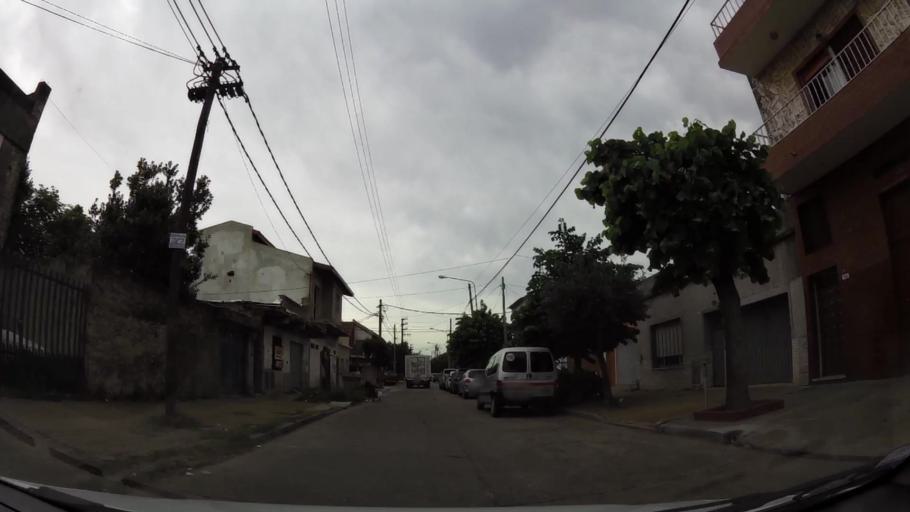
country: AR
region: Buenos Aires
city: San Justo
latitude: -34.6680
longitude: -58.5270
